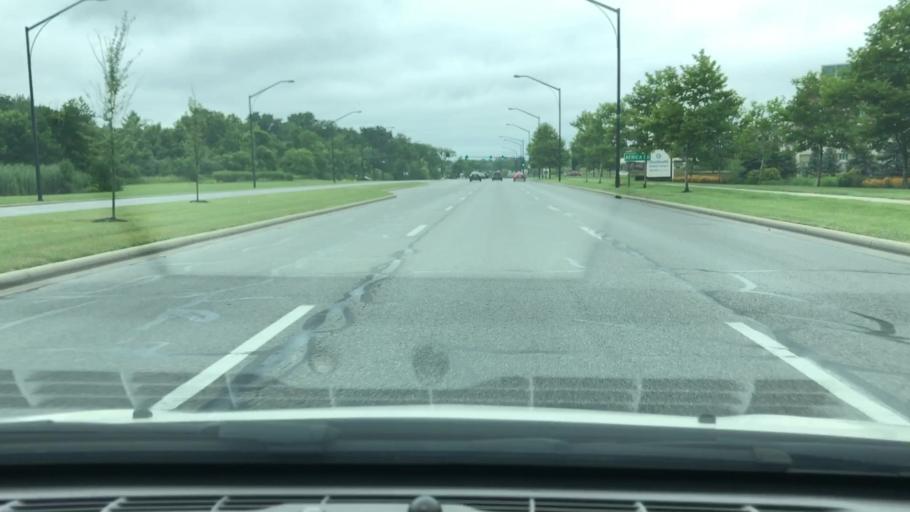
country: US
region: Ohio
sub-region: Franklin County
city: Westerville
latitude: 40.1461
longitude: -82.9361
